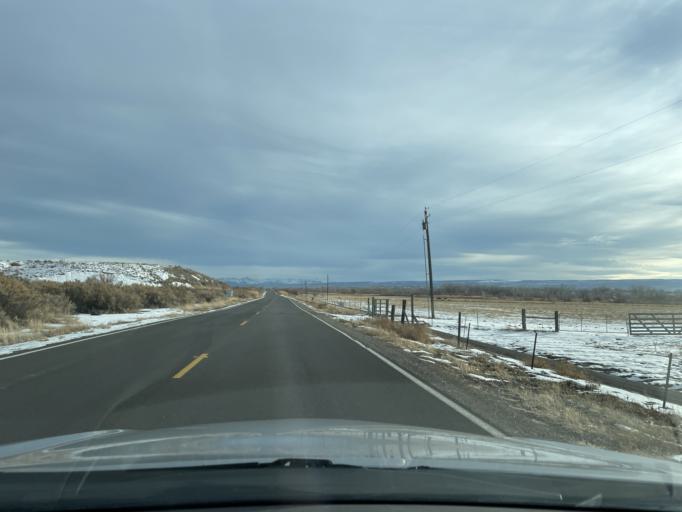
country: US
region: Colorado
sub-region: Montrose County
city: Olathe
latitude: 38.6556
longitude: -107.9970
